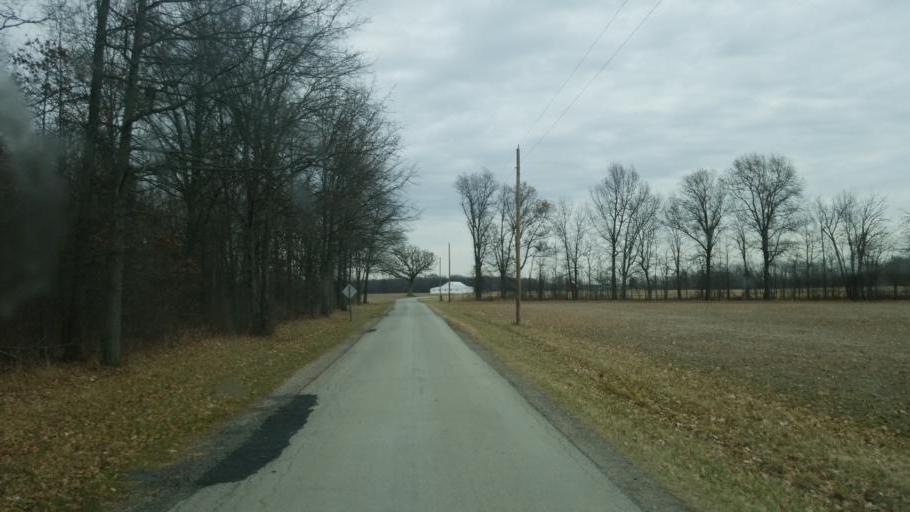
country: US
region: Ohio
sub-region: Wyandot County
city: Upper Sandusky
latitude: 40.7229
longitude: -83.3493
